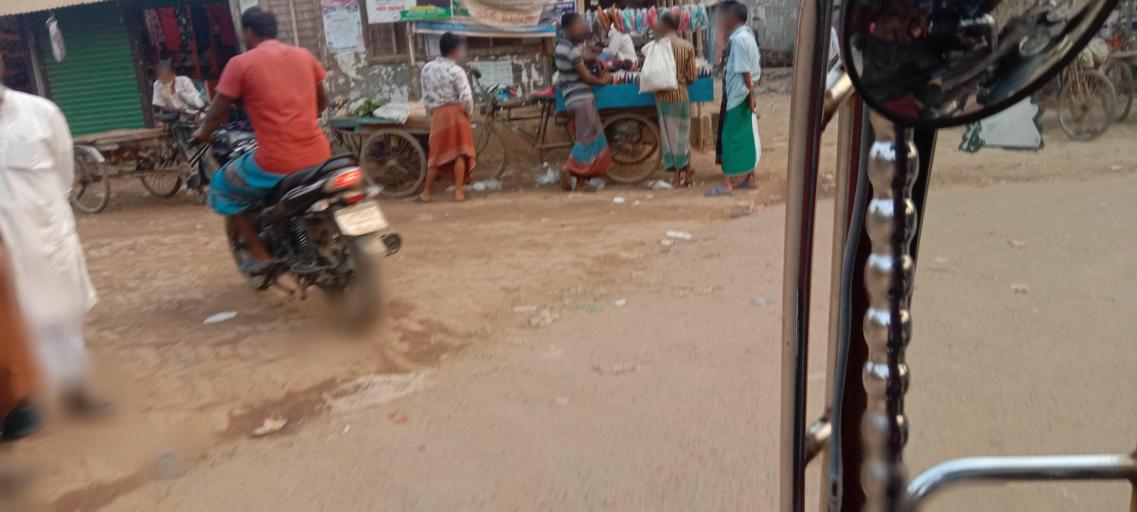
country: BD
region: Dhaka
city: Sakhipur
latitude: 24.4271
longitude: 90.2641
